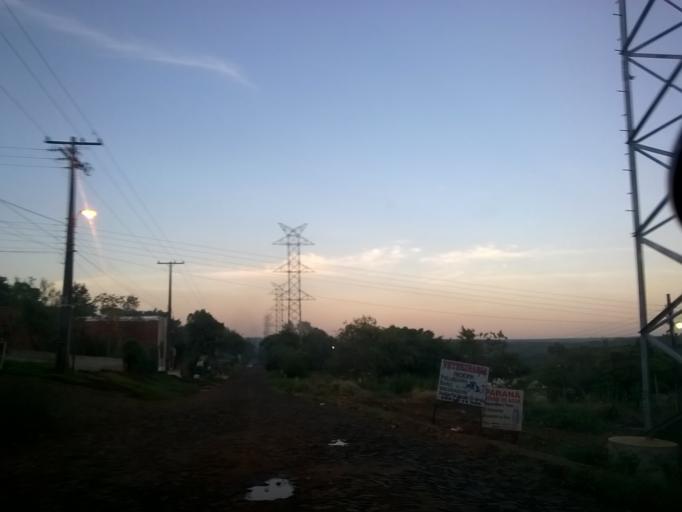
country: PY
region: Alto Parana
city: Ciudad del Este
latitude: -25.4838
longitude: -54.6454
